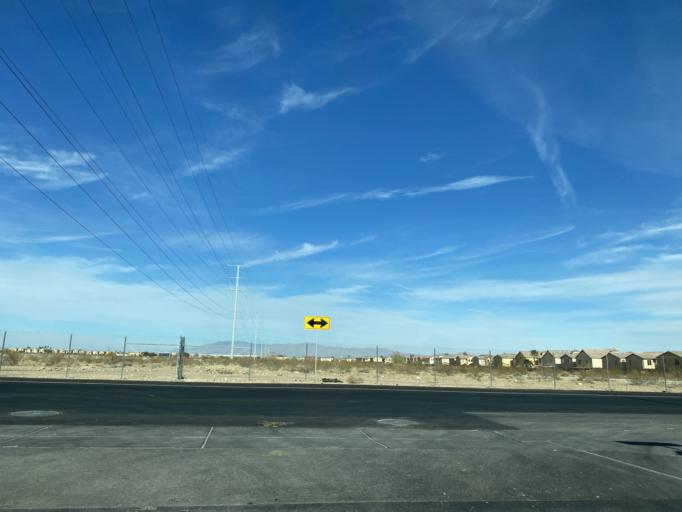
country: US
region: Nevada
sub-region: Clark County
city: Enterprise
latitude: 36.0421
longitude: -115.2124
